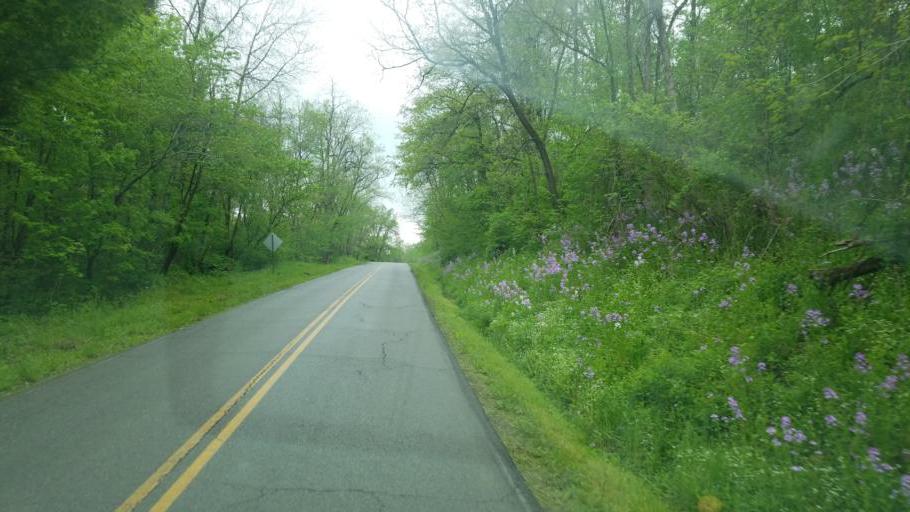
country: US
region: Ohio
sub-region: Harrison County
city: Cadiz
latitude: 40.2725
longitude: -80.9015
